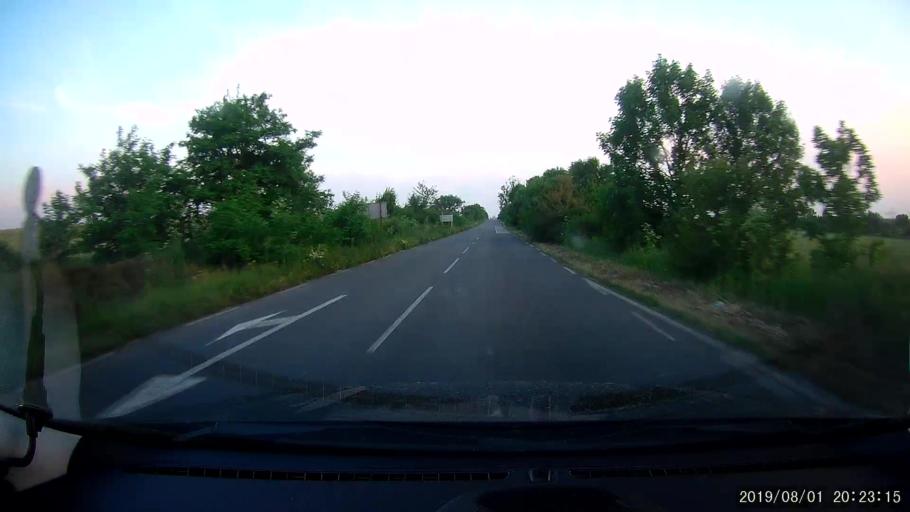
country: BG
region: Yambol
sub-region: Obshtina Elkhovo
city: Elkhovo
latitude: 42.2523
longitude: 26.5988
